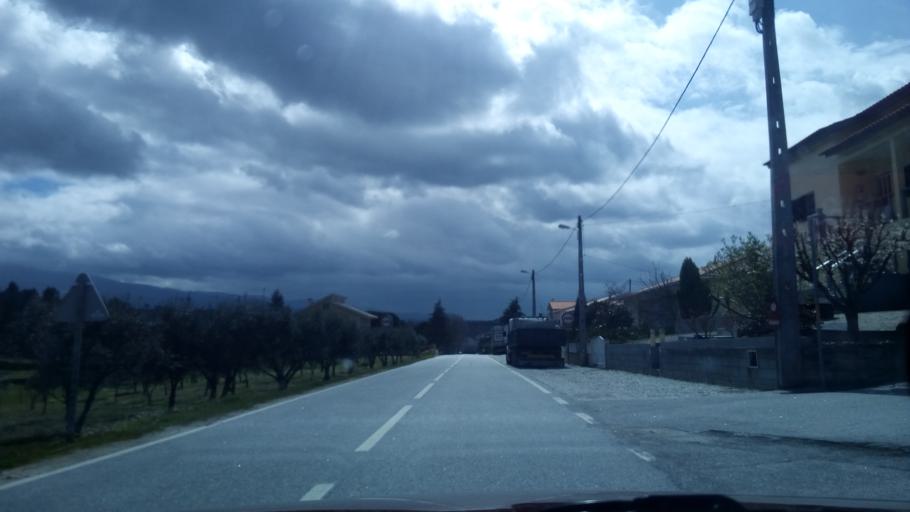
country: PT
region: Guarda
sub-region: Fornos de Algodres
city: Fornos de Algodres
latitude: 40.5927
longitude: -7.5353
